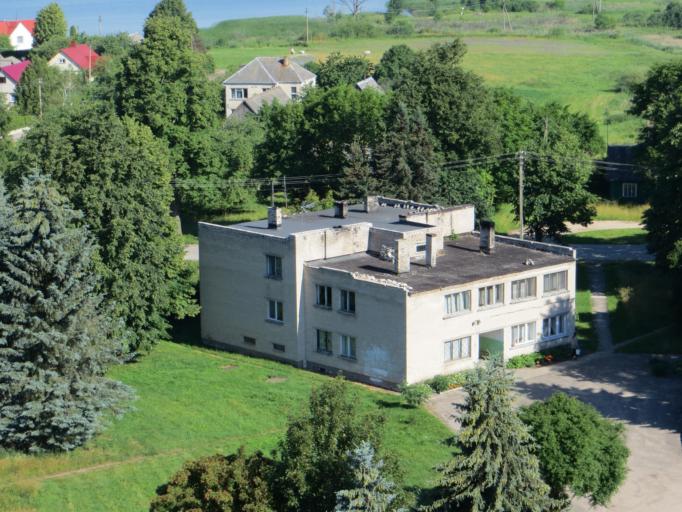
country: LT
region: Alytaus apskritis
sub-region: Alytaus rajonas
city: Daugai
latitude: 54.3882
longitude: 24.3767
